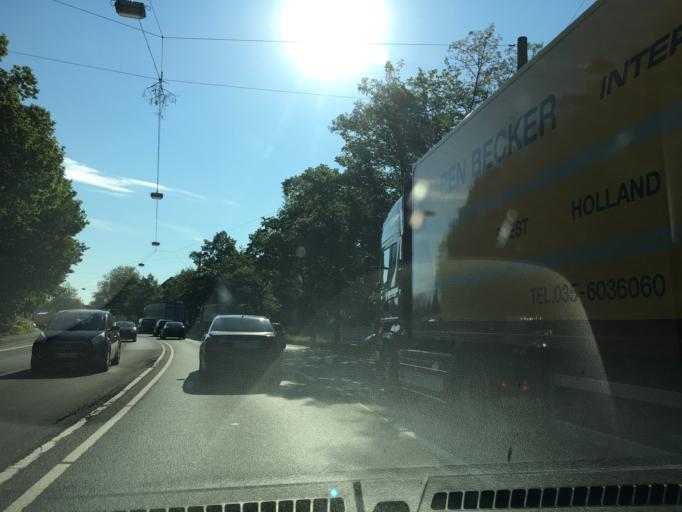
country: DE
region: North Rhine-Westphalia
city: Bad Oeynhausen
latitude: 52.2059
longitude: 8.7979
